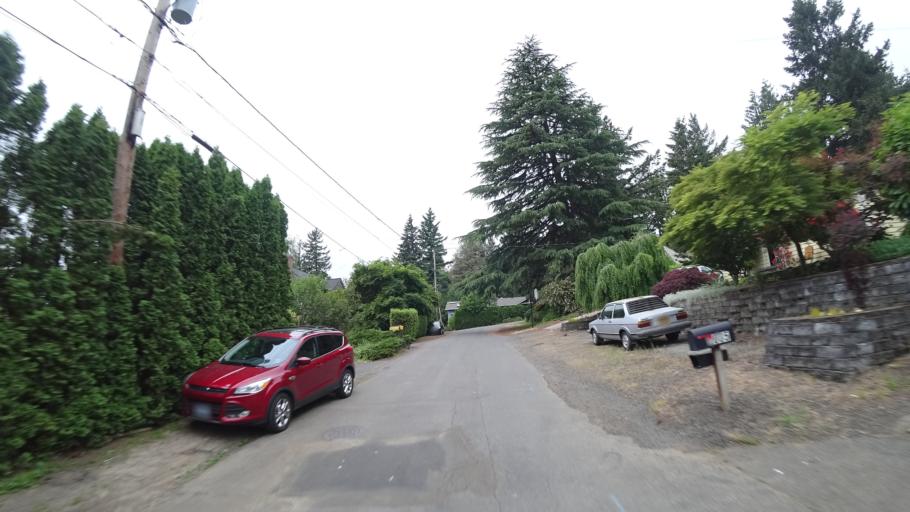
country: US
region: Oregon
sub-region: Multnomah County
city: Portland
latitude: 45.4868
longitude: -122.7046
